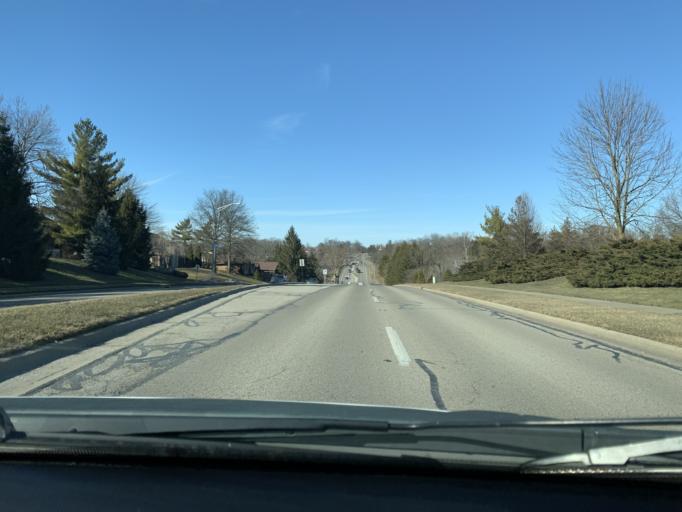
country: US
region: Ohio
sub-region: Montgomery County
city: Centerville
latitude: 39.6393
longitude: -84.1385
